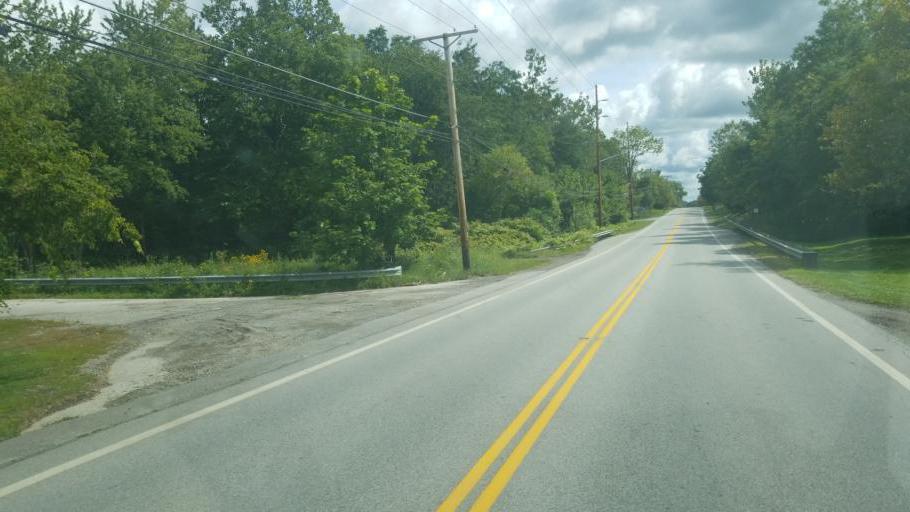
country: US
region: Ohio
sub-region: Lorain County
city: Oberlin
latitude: 41.2939
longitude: -82.1873
